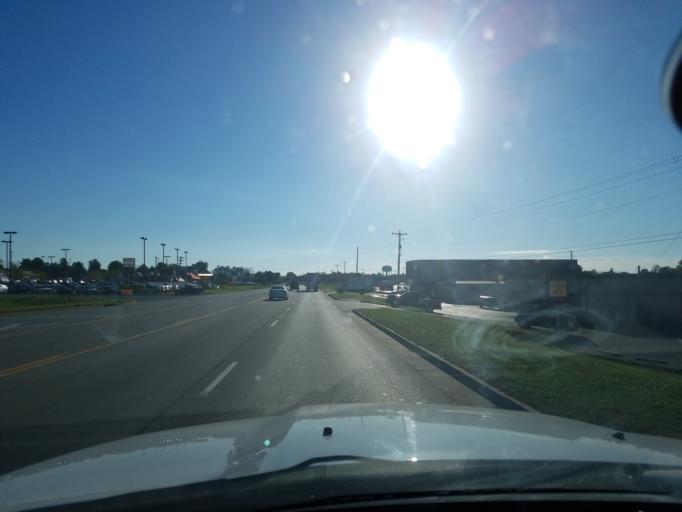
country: US
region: Kentucky
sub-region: Nelson County
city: Bardstown
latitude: 37.8271
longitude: -85.4680
